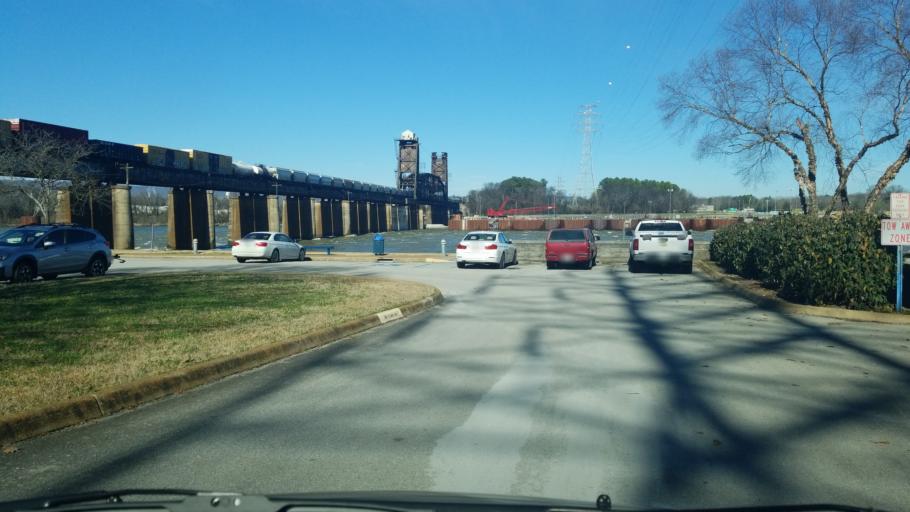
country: US
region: Tennessee
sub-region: Hamilton County
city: East Chattanooga
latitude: 35.1020
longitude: -85.2323
